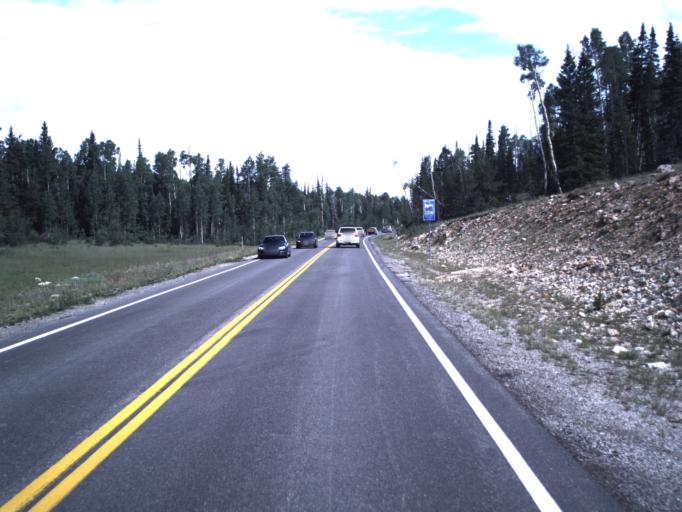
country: US
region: Utah
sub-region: Iron County
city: Parowan
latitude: 37.5440
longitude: -112.7851
